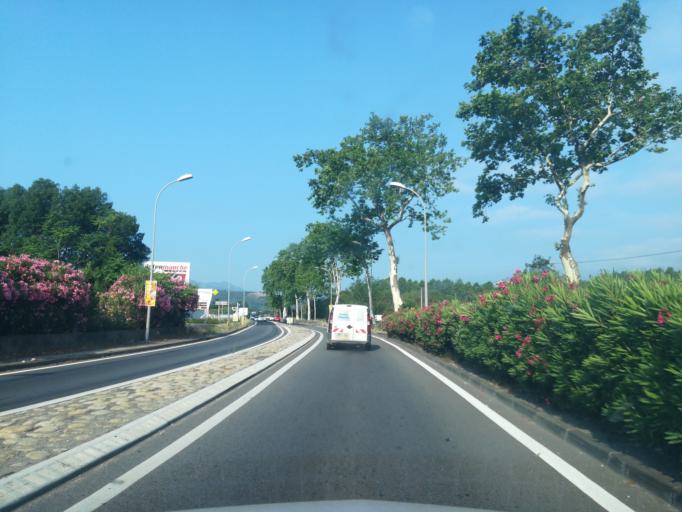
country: FR
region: Languedoc-Roussillon
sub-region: Departement des Pyrenees-Orientales
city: Ceret
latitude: 42.5021
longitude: 2.7586
